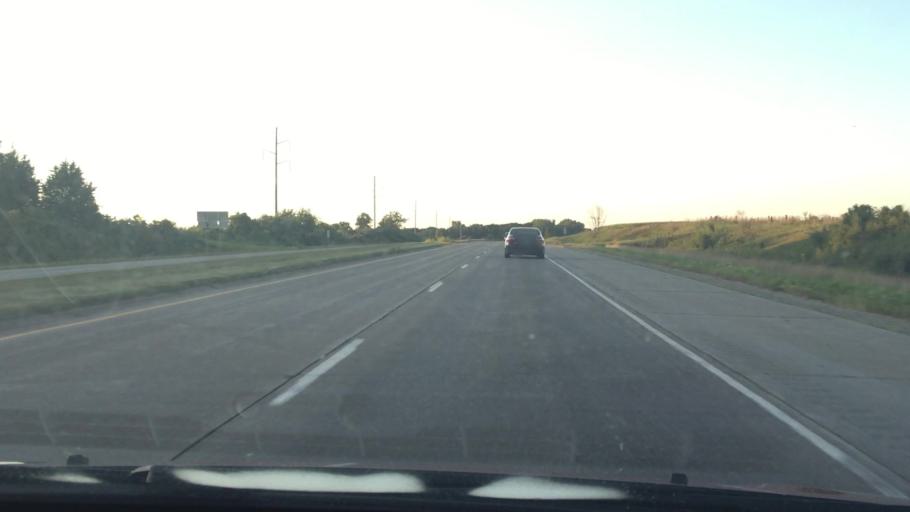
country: US
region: Iowa
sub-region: Muscatine County
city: Muscatine
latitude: 41.4384
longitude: -91.0918
